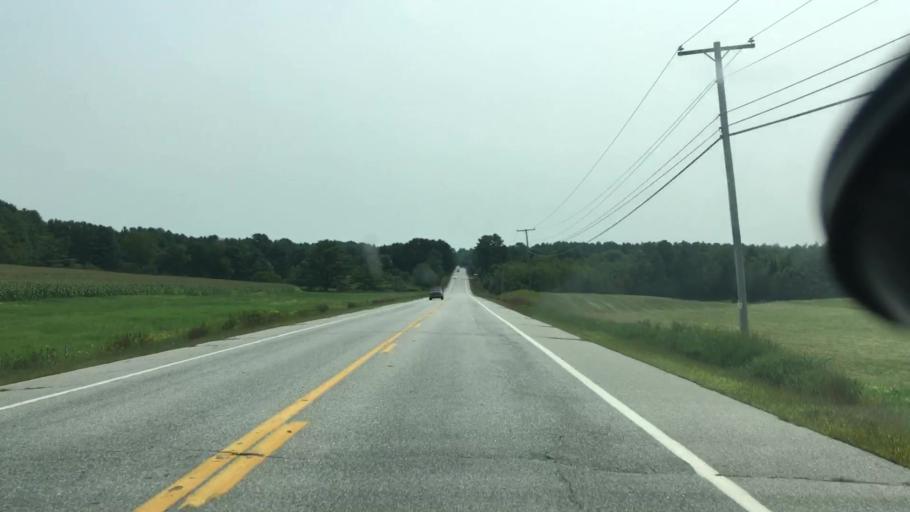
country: US
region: Maine
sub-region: Androscoggin County
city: Livermore Falls
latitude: 44.4108
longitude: -70.1404
